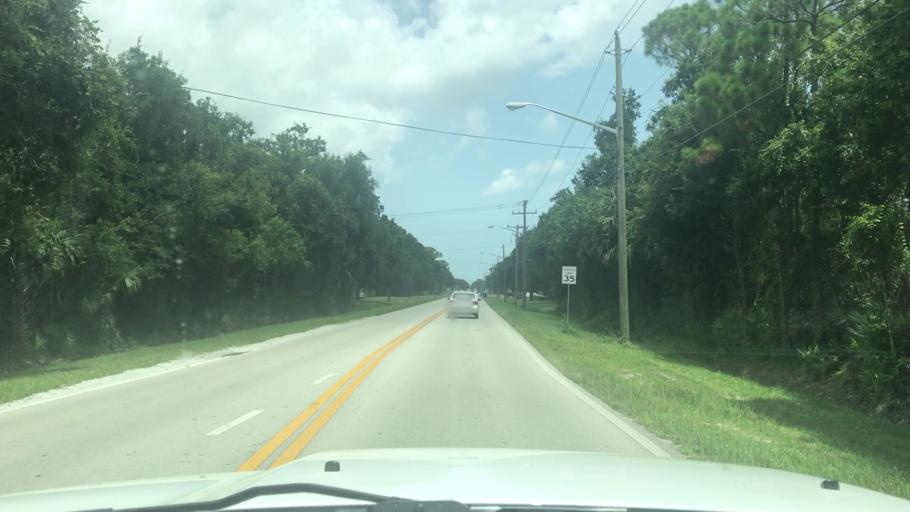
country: US
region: Florida
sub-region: Indian River County
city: Vero Beach South
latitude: 27.6320
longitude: -80.4302
